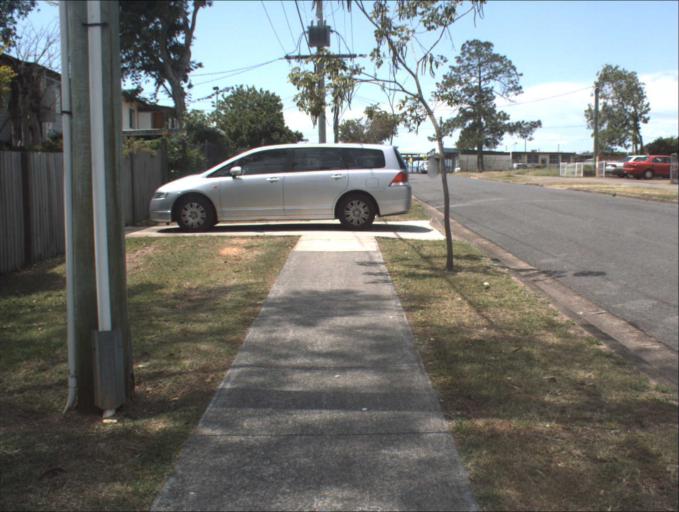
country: AU
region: Queensland
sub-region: Logan
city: Logan City
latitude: -27.6394
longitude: 153.1029
